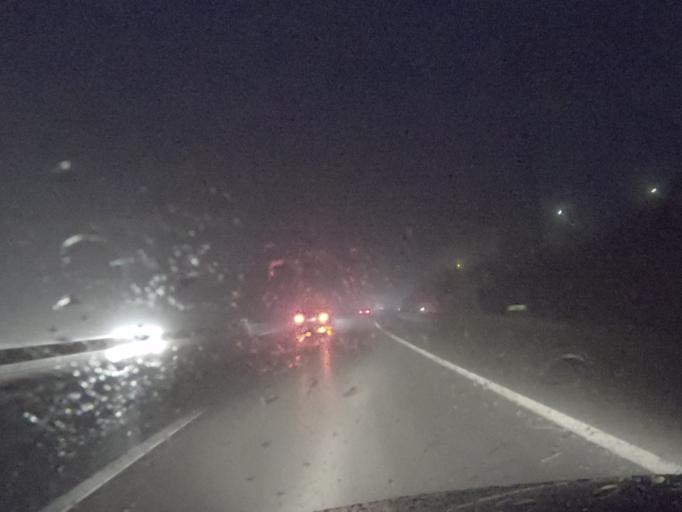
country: PT
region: Vila Real
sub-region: Santa Marta de Penaguiao
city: Santa Marta de Penaguiao
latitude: 41.2285
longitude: -7.7350
